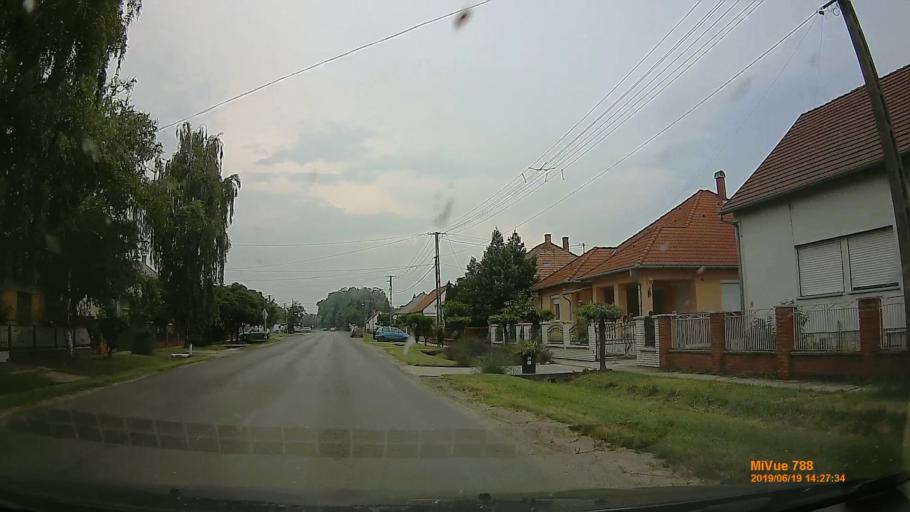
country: HU
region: Baranya
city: Szigetvar
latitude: 46.0439
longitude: 17.7818
